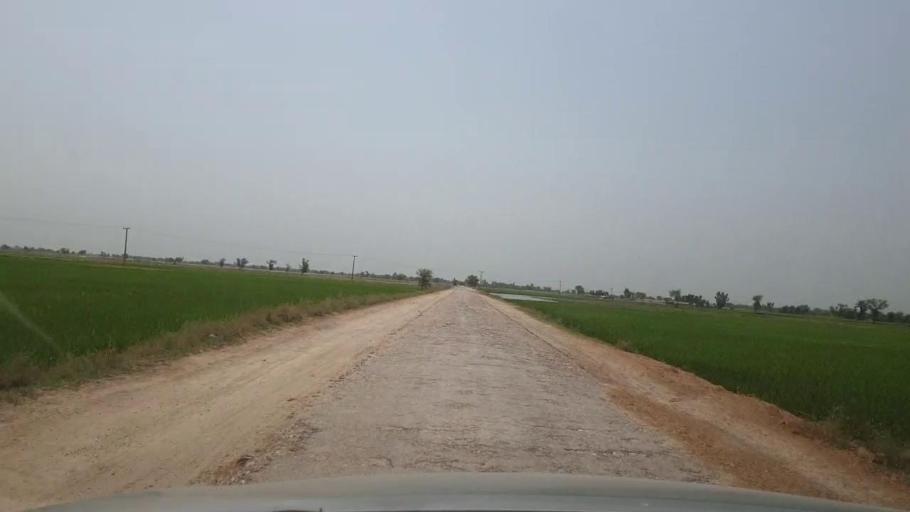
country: PK
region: Sindh
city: Garhi Yasin
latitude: 27.9189
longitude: 68.4040
